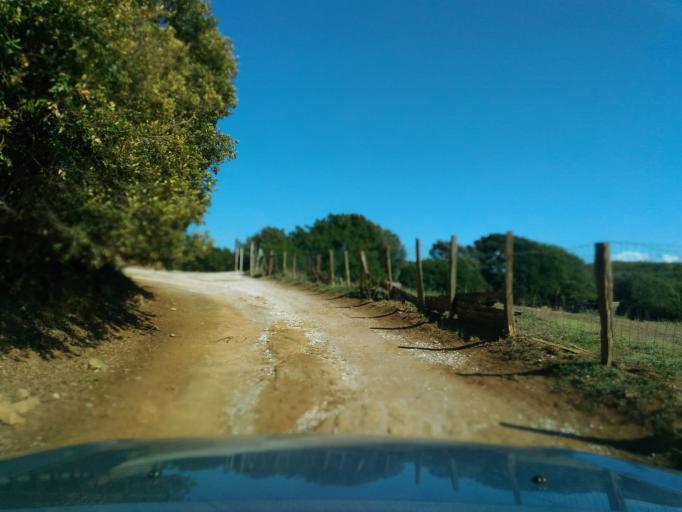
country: FR
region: Corsica
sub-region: Departement de la Haute-Corse
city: Brando
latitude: 42.9654
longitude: 9.4485
